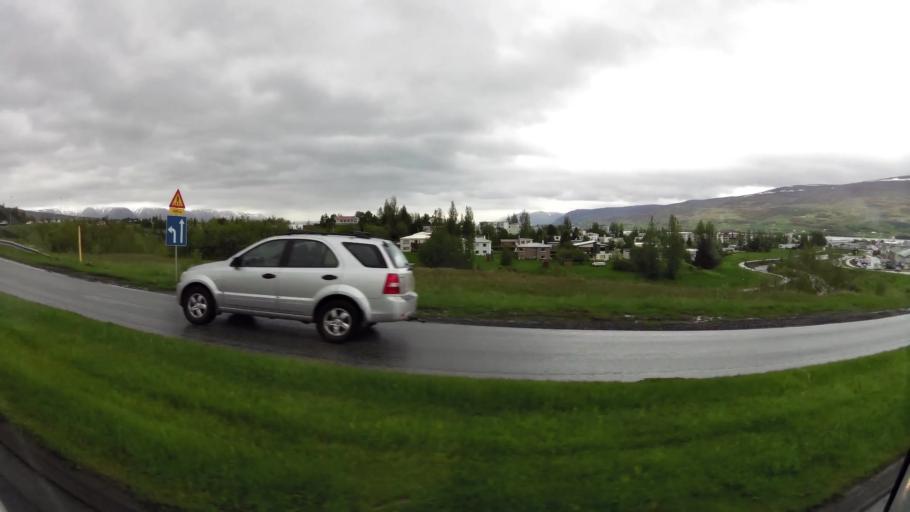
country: IS
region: Northeast
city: Akureyri
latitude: 65.6856
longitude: -18.1128
